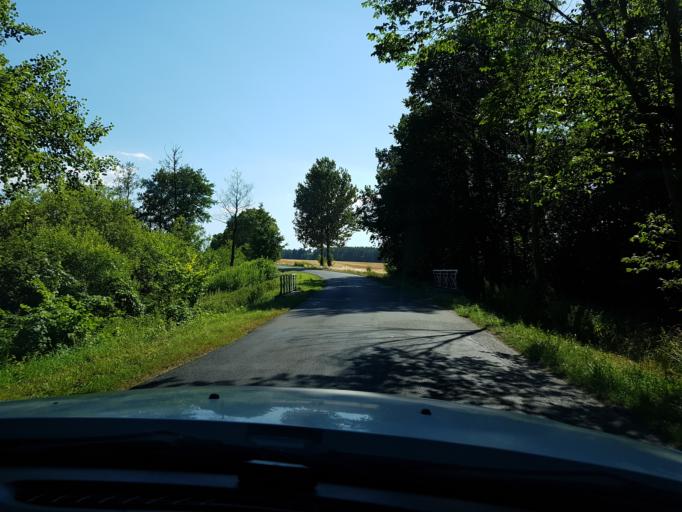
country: PL
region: West Pomeranian Voivodeship
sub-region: Powiat bialogardzki
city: Karlino
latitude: 53.9747
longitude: 15.9109
